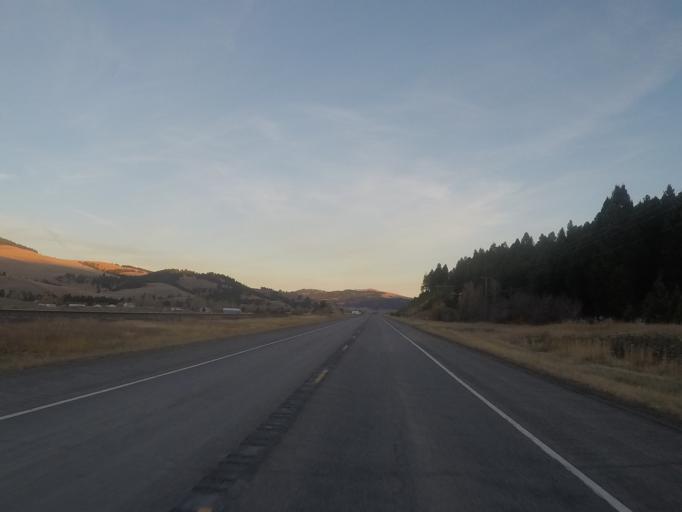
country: US
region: Montana
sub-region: Powell County
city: Deer Lodge
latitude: 46.5659
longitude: -112.4521
